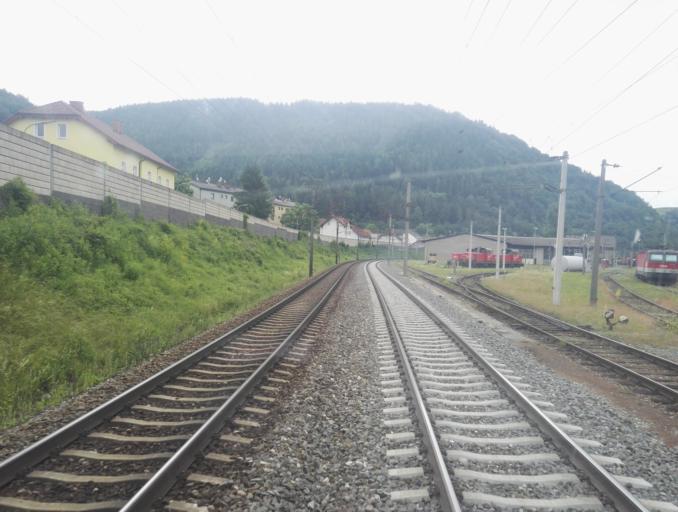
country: AT
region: Styria
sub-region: Politischer Bezirk Bruck-Muerzzuschlag
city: Bruck an der Mur
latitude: 47.4270
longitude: 15.2766
